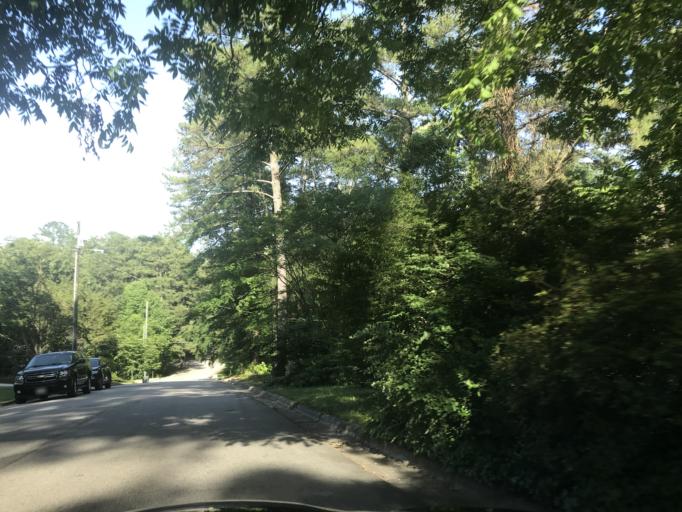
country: US
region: North Carolina
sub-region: Wake County
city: West Raleigh
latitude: 35.8058
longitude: -78.6757
